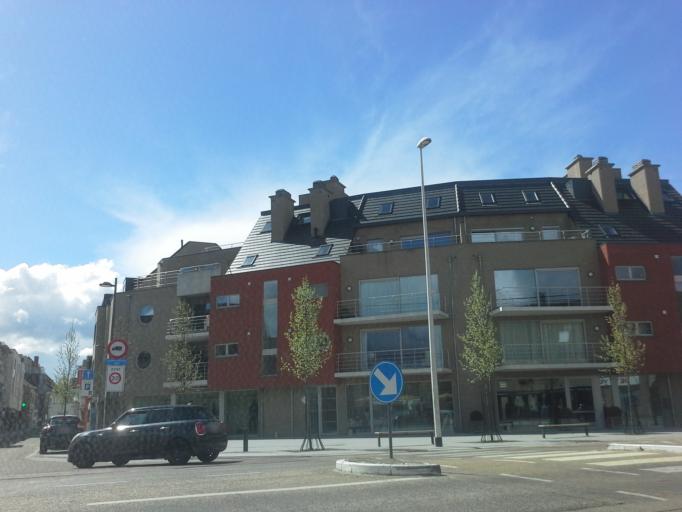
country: BE
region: Flanders
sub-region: Provincie Limburg
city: Tessenderlo
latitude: 51.0699
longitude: 5.0885
